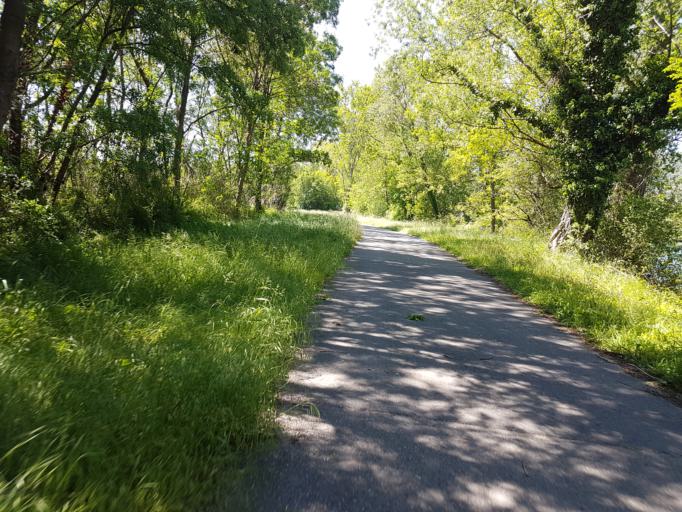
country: FR
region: Rhone-Alpes
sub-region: Departement de la Drome
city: Andancette
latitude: 45.2587
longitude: 4.8106
